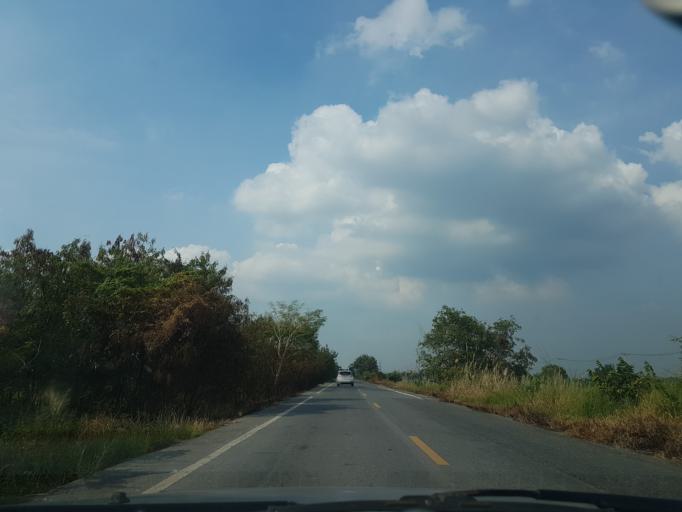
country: TH
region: Phra Nakhon Si Ayutthaya
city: Phachi
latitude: 14.4241
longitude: 100.7788
